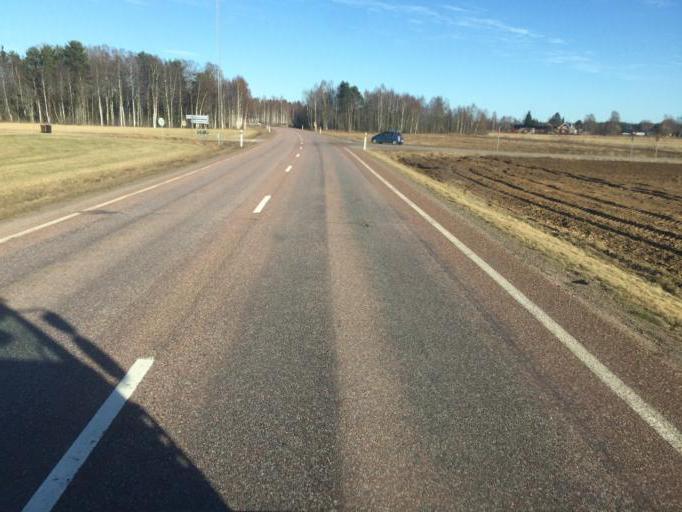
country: SE
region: Dalarna
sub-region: Vansbro Kommun
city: Jarna
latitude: 60.5469
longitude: 14.3769
